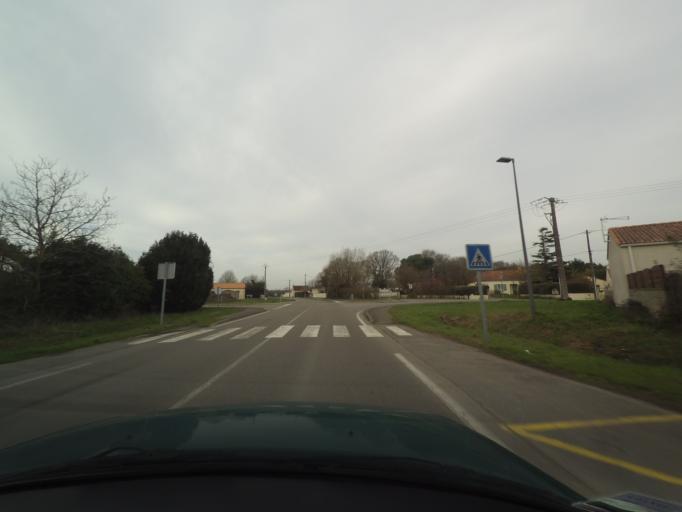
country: FR
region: Pays de la Loire
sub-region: Departement de la Loire-Atlantique
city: Arthon-en-Retz
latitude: 47.1196
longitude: -1.9524
